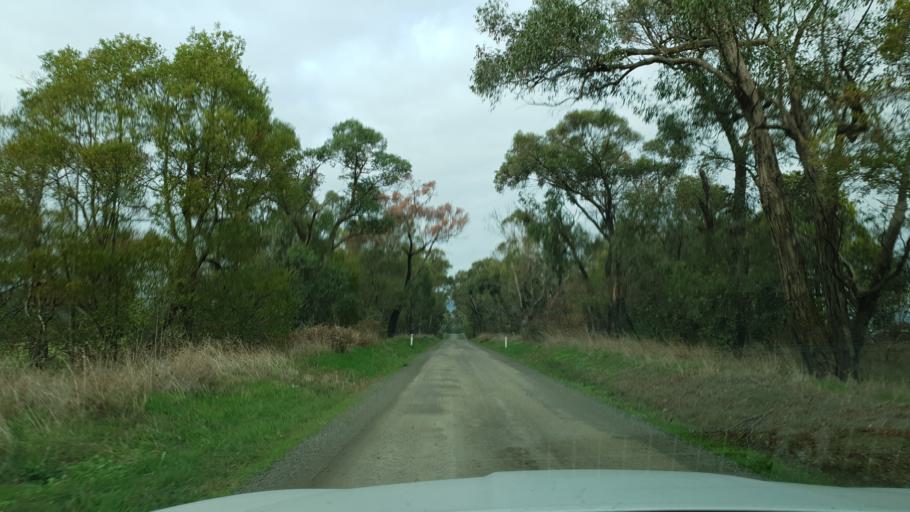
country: AU
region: Victoria
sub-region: Latrobe
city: Moe
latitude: -38.1695
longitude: 146.1313
